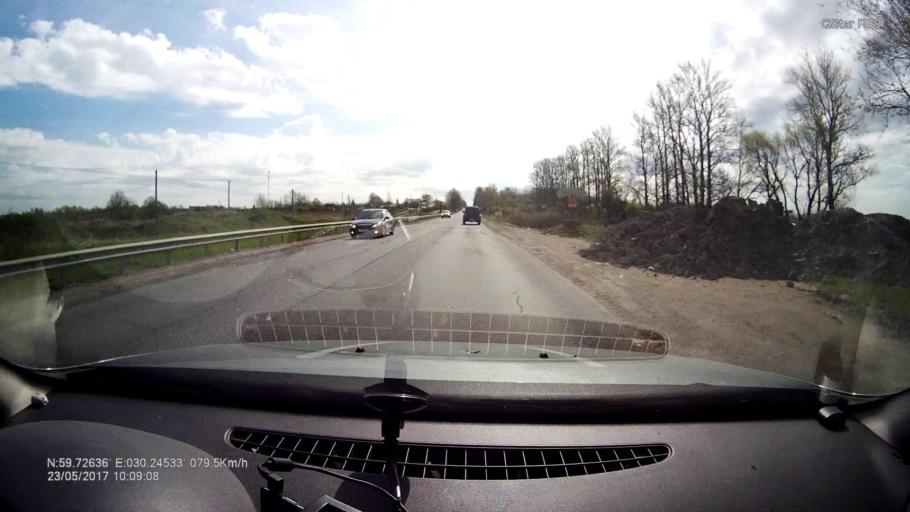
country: RU
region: St.-Petersburg
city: Aleksandrovskaya
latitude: 59.7263
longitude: 30.2450
